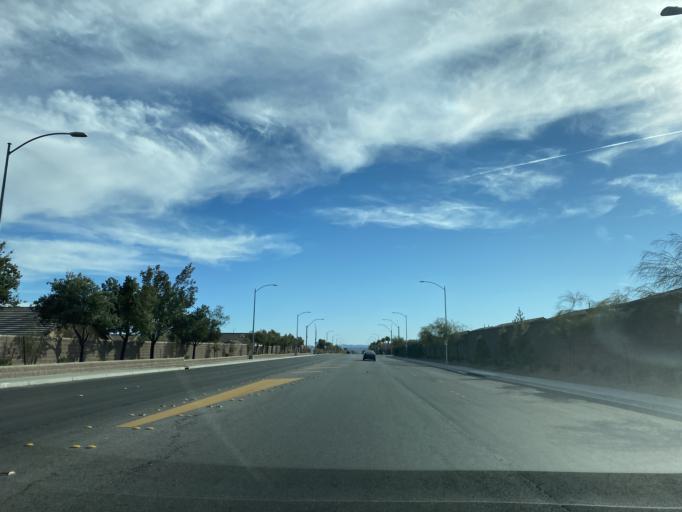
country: US
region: Nevada
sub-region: Clark County
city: Summerlin South
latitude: 36.2937
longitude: -115.3059
